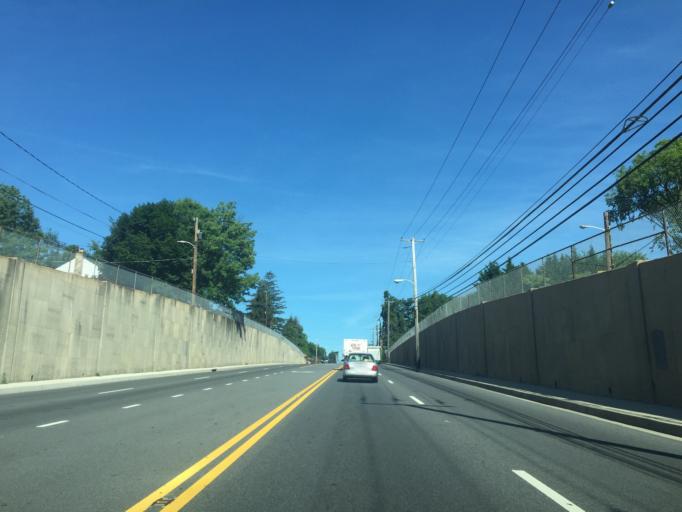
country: US
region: Maryland
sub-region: Baltimore County
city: Lochearn
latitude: 39.3380
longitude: -76.7154
